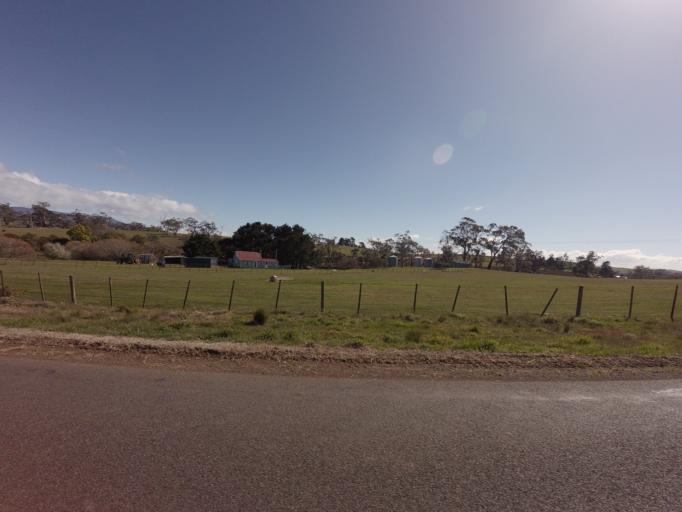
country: AU
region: Tasmania
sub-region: Northern Midlands
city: Evandale
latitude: -41.9069
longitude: 147.3930
